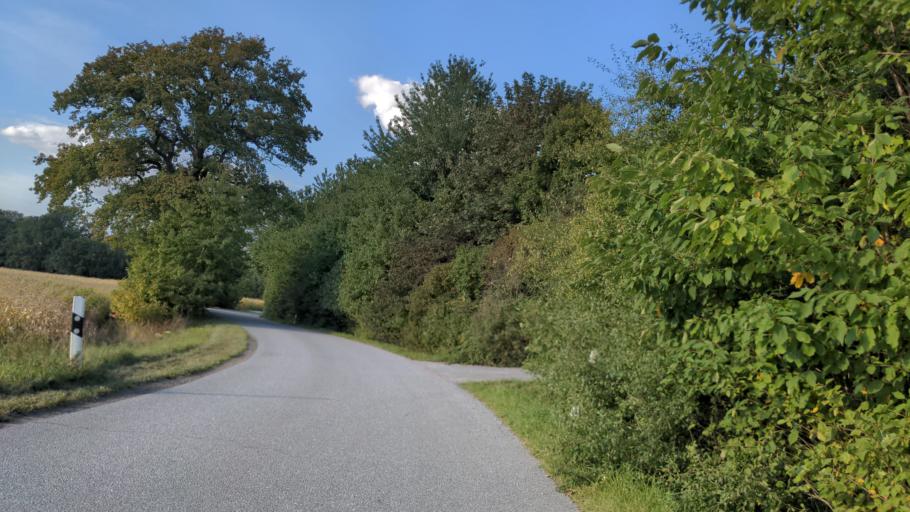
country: DE
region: Schleswig-Holstein
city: Ahrensbok
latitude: 53.9855
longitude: 10.6261
